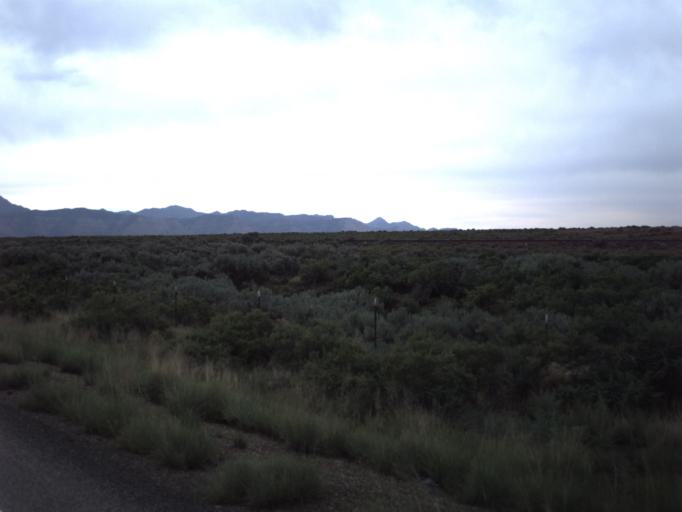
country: US
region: Utah
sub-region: Carbon County
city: East Carbon City
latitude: 39.5311
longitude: -110.5546
